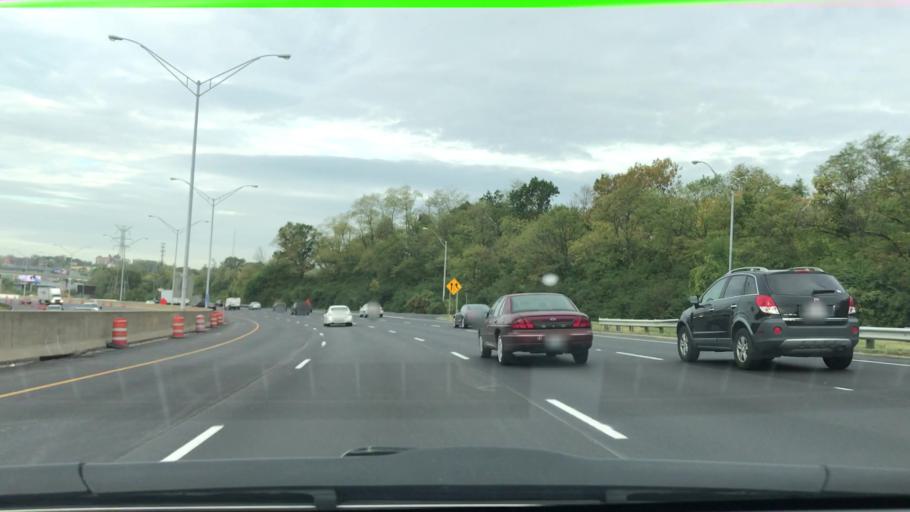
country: US
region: Ohio
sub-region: Hamilton County
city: Norwood
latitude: 39.1441
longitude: -84.4806
